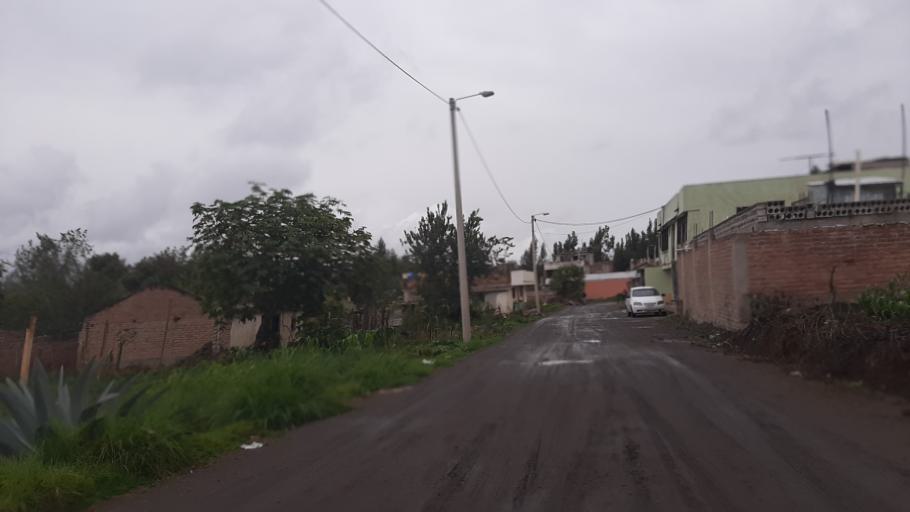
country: EC
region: Chimborazo
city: Riobamba
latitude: -1.6552
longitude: -78.6373
